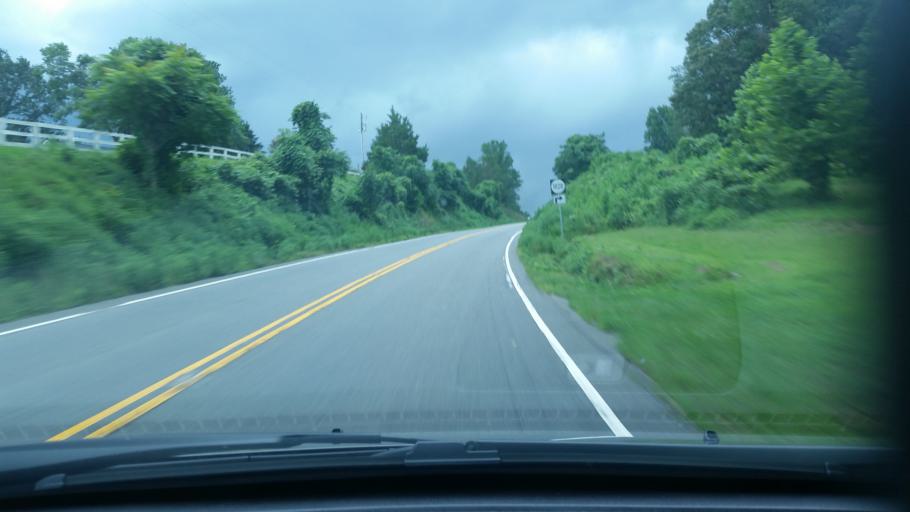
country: US
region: Virginia
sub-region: Nelson County
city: Nellysford
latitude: 37.8783
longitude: -78.8218
